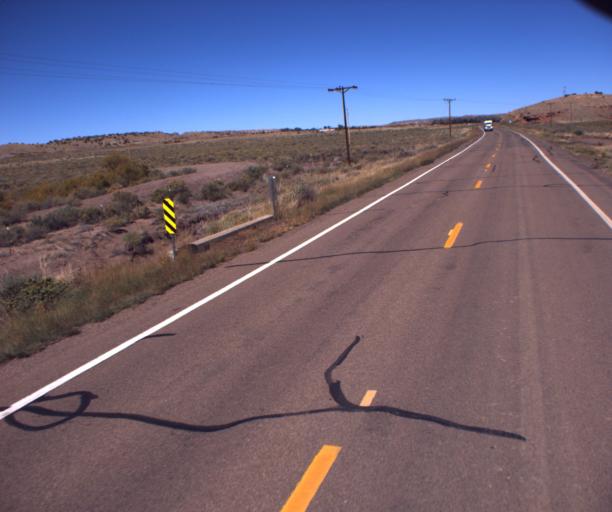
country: US
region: Arizona
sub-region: Apache County
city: Saint Johns
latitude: 34.4166
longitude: -109.4107
